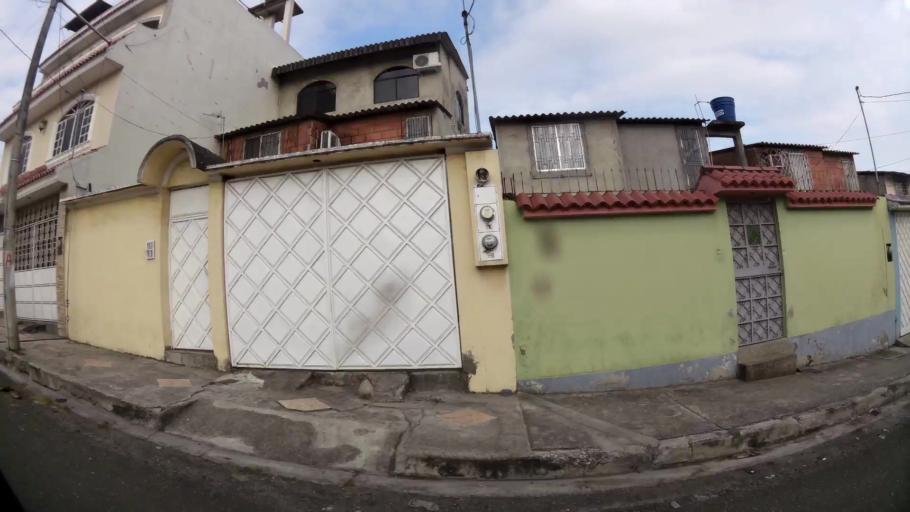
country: EC
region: Guayas
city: Eloy Alfaro
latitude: -2.1318
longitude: -79.8957
